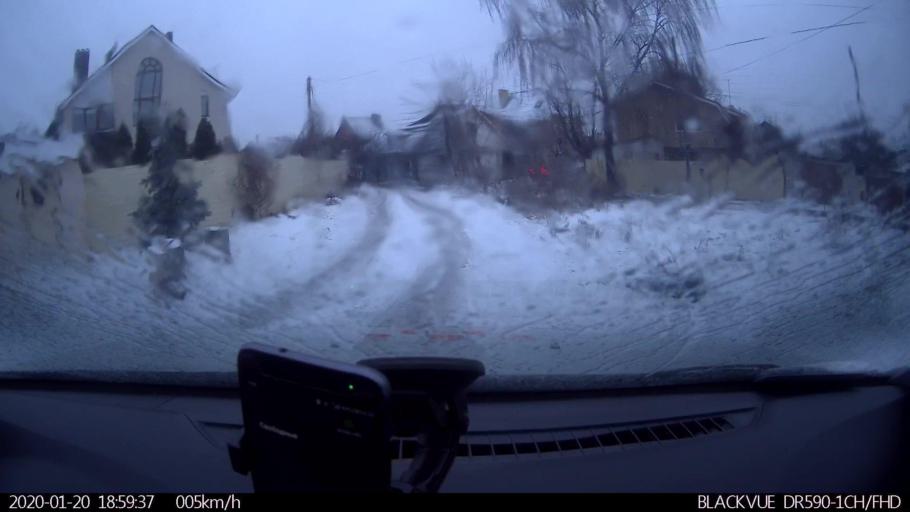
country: RU
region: Nizjnij Novgorod
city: Nizhniy Novgorod
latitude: 56.2969
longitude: 44.0242
